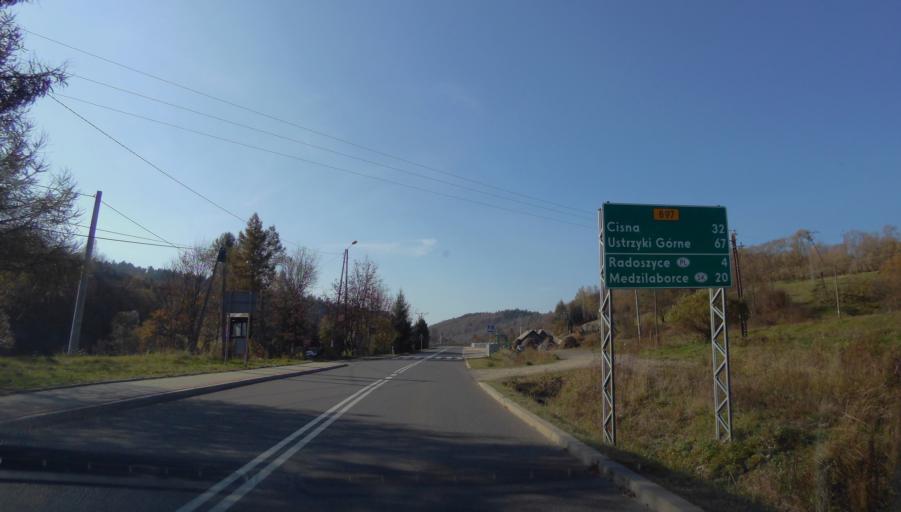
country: PL
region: Subcarpathian Voivodeship
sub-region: Powiat sanocki
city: Komancza
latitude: 49.3346
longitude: 22.0692
